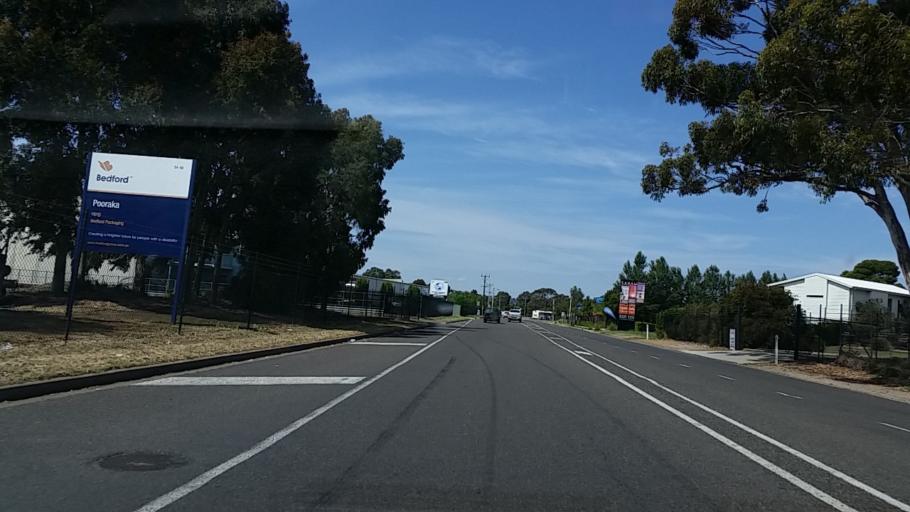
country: AU
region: South Australia
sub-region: Salisbury
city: Ingle Farm
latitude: -34.8270
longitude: 138.6128
